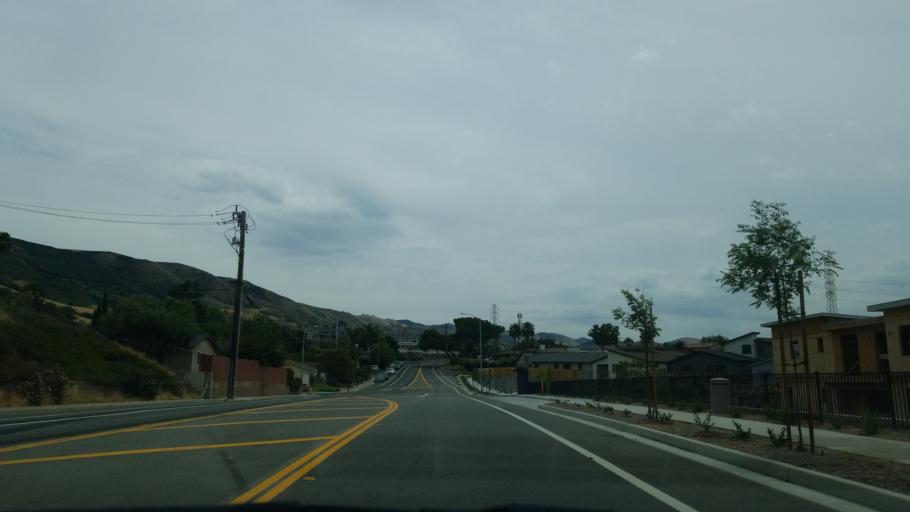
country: US
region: California
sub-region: San Luis Obispo County
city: San Luis Obispo
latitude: 35.2613
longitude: -120.6385
